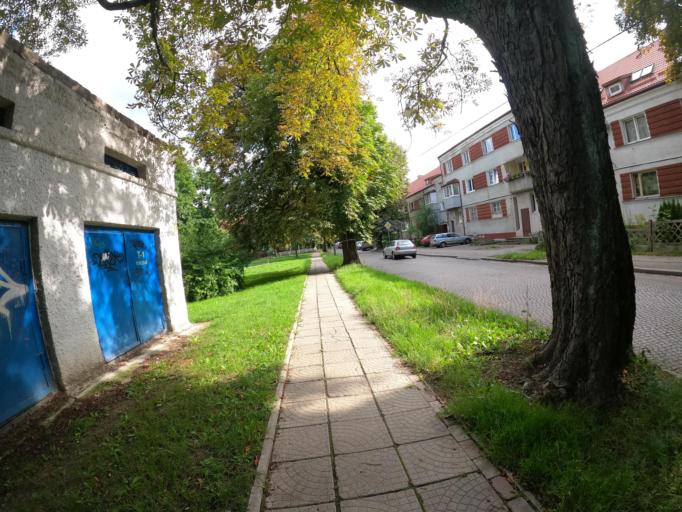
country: RU
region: Kaliningrad
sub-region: Gorod Kaliningrad
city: Kaliningrad
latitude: 54.7281
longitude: 20.4684
